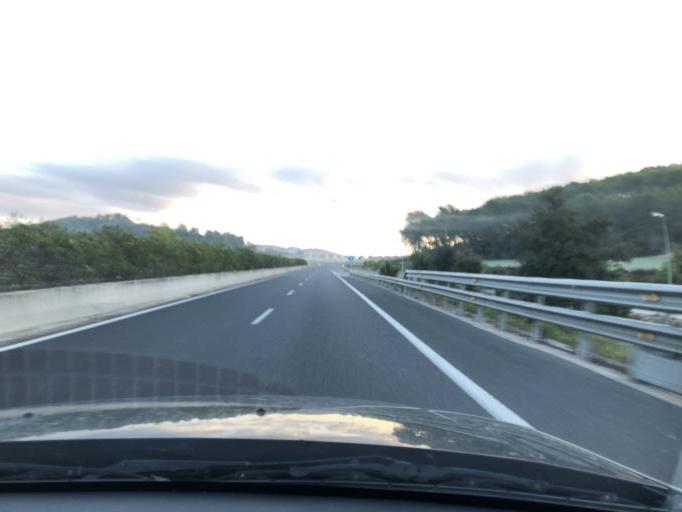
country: ES
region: Balearic Islands
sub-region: Illes Balears
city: Sant Joan
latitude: 39.5638
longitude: 3.0376
